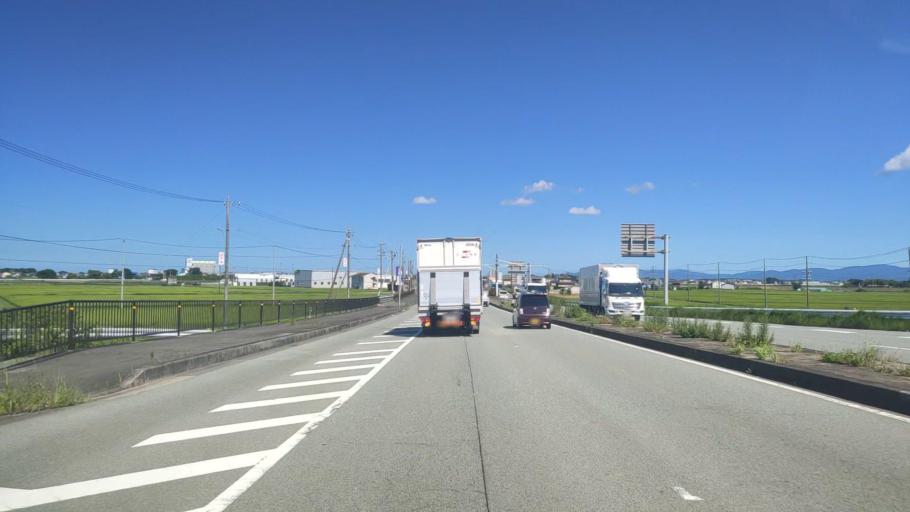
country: JP
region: Mie
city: Hisai-motomachi
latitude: 34.5856
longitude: 136.5551
